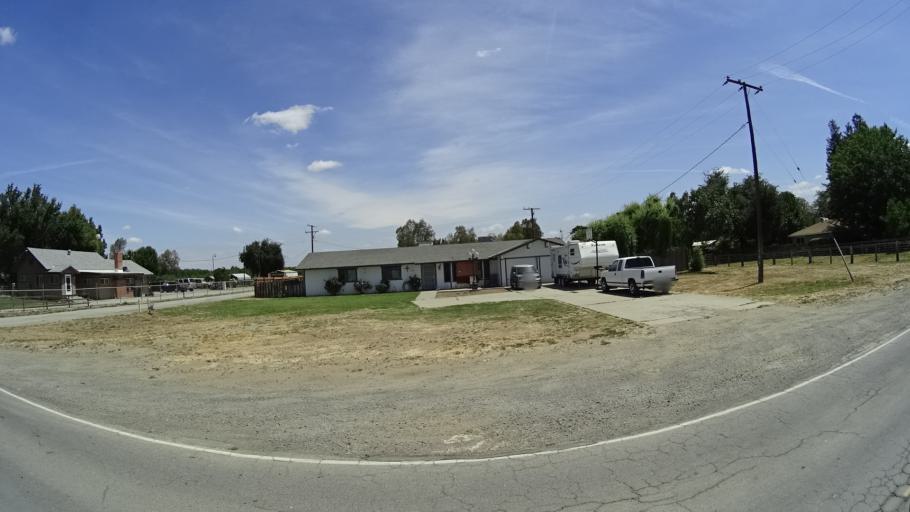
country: US
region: California
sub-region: Kings County
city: Home Garden
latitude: 36.2863
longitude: -119.6728
